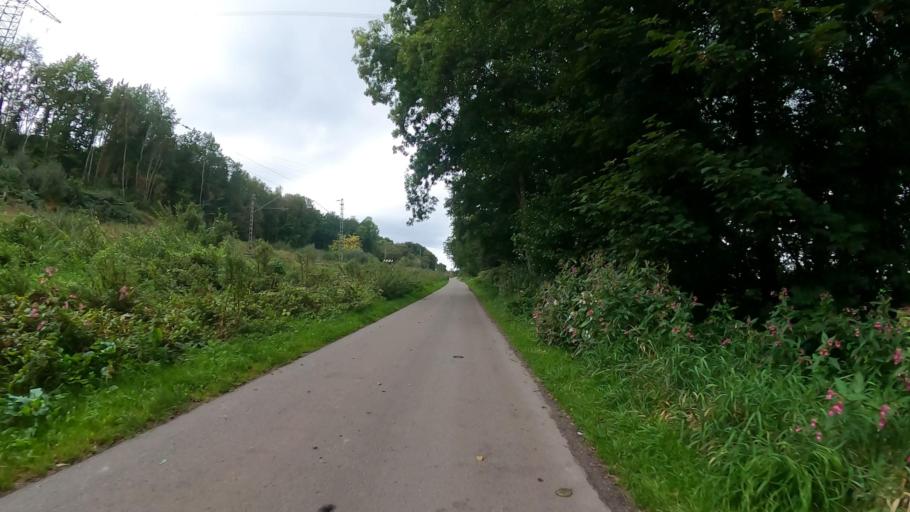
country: DE
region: Lower Saxony
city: Agathenburg
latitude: 53.5569
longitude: 9.5452
